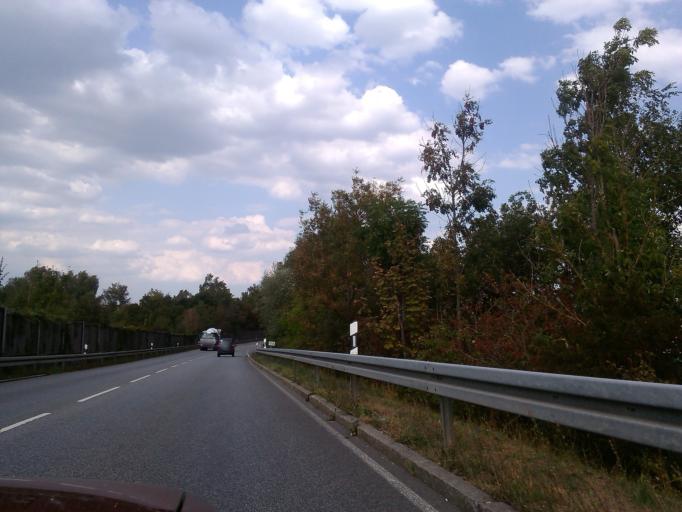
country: DE
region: Bavaria
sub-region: Upper Bavaria
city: Puchheim
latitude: 48.1714
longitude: 11.3604
